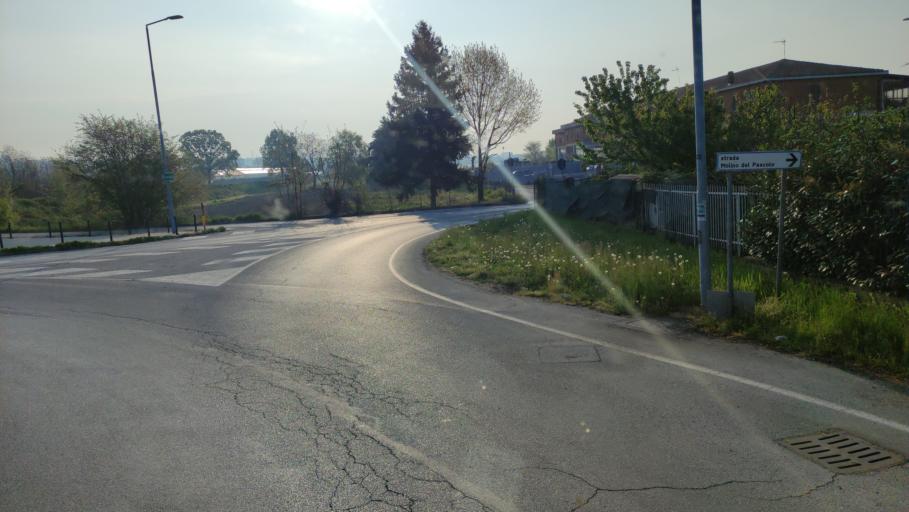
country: IT
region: Piedmont
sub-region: Provincia di Torino
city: Moncalieri
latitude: 44.9891
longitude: 7.7034
